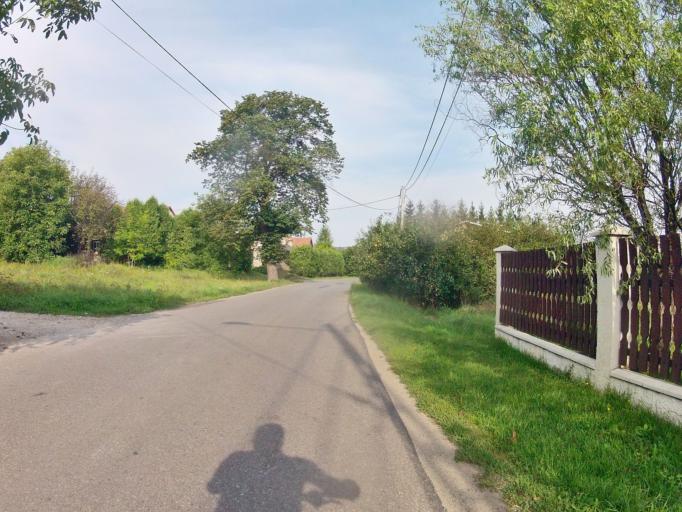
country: PL
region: Subcarpathian Voivodeship
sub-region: Powiat jasielski
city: Jaslo
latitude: 49.7372
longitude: 21.4514
